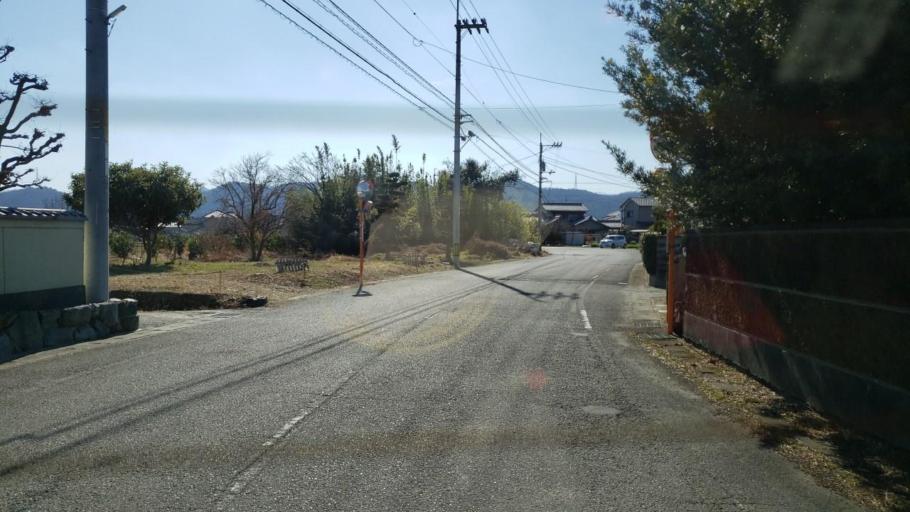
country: JP
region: Tokushima
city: Ishii
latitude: 34.0780
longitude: 134.4292
